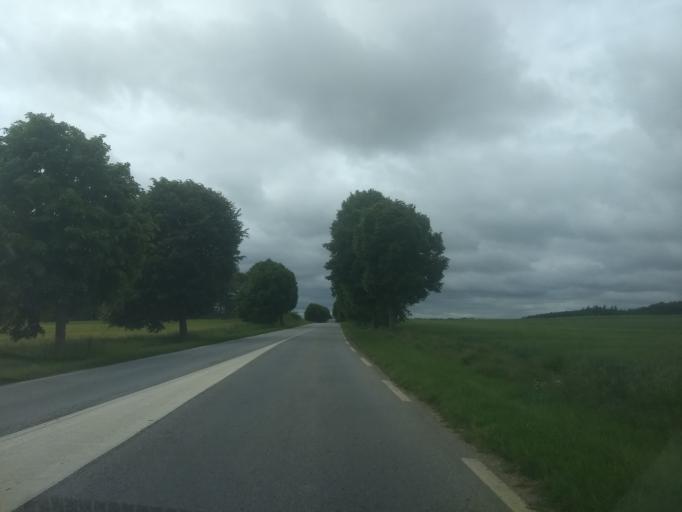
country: FR
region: Centre
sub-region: Departement d'Eure-et-Loir
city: Treon
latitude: 48.6640
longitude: 1.3095
